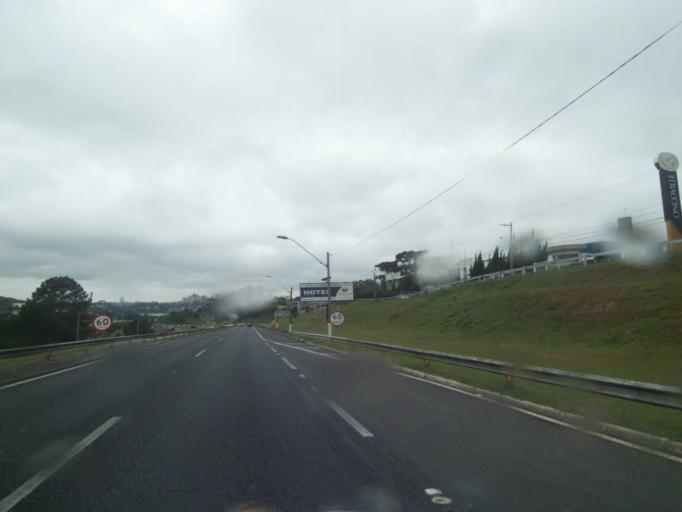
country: BR
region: Parana
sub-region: Curitiba
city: Curitiba
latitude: -25.4309
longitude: -49.3278
